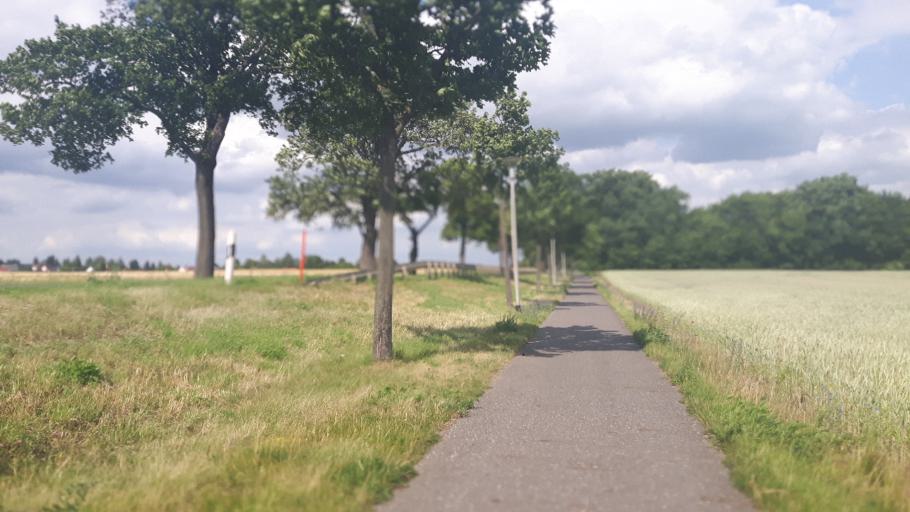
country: DE
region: Brandenburg
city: Bernau bei Berlin
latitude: 52.6346
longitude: 13.5535
